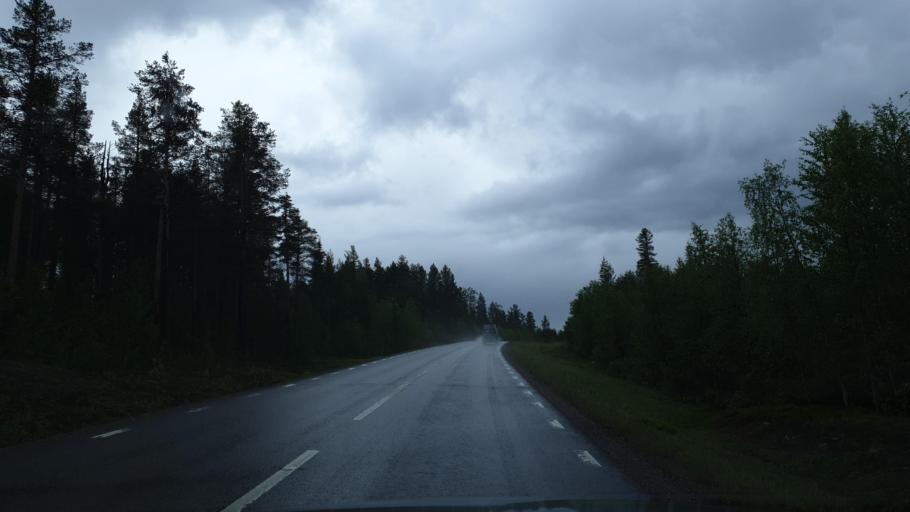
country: SE
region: Norrbotten
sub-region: Gallivare Kommun
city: Malmberget
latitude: 67.3538
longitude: 21.0977
